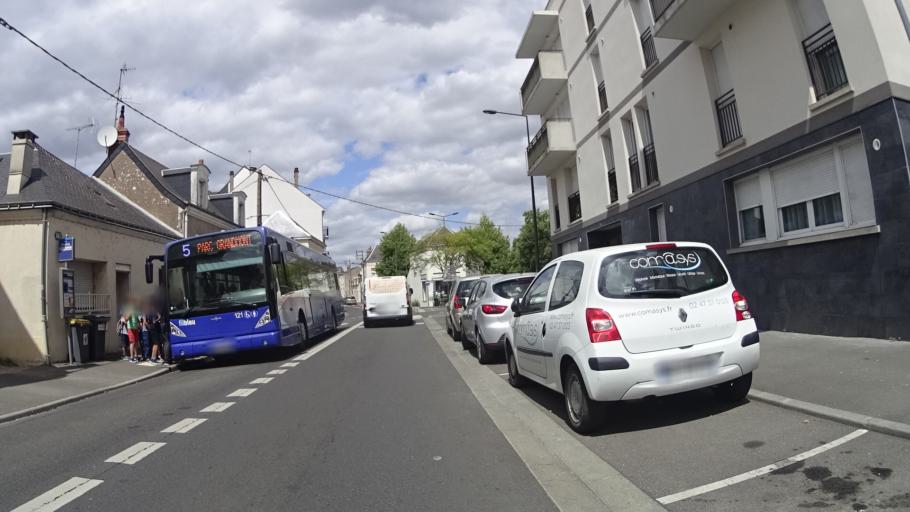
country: FR
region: Centre
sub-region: Departement d'Indre-et-Loire
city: Tours
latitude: 47.3788
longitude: 0.6798
